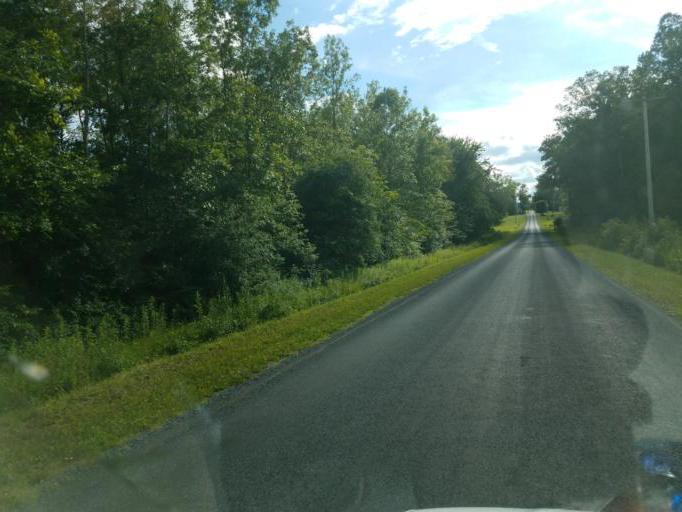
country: US
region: New York
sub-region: Wayne County
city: Clyde
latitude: 43.0453
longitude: -76.8682
